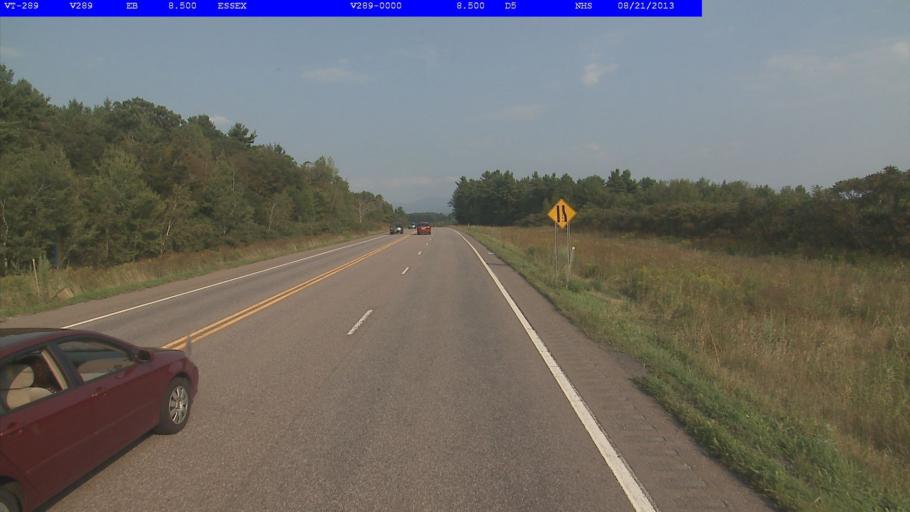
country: US
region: Vermont
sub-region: Chittenden County
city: Essex Junction
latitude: 44.5144
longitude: -73.1042
